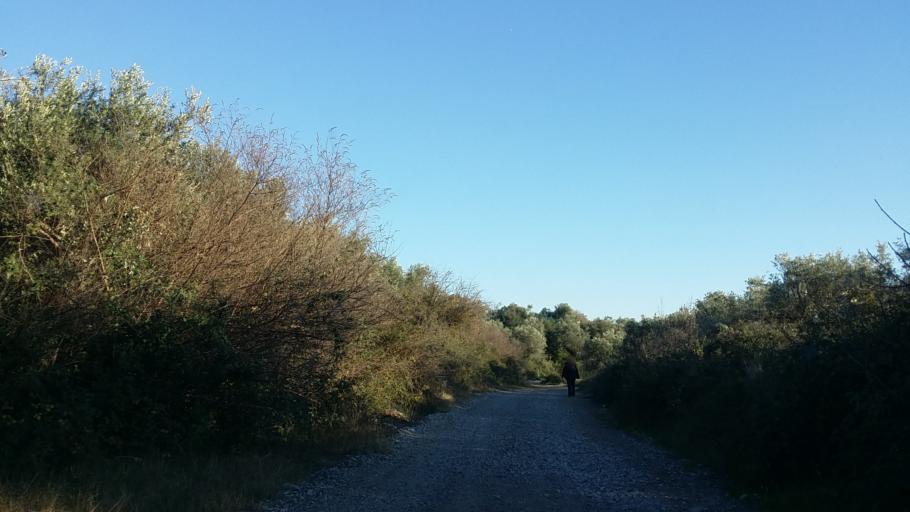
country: GR
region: West Greece
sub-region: Nomos Aitolias kai Akarnanias
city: Lepenou
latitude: 38.6709
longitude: 21.3102
